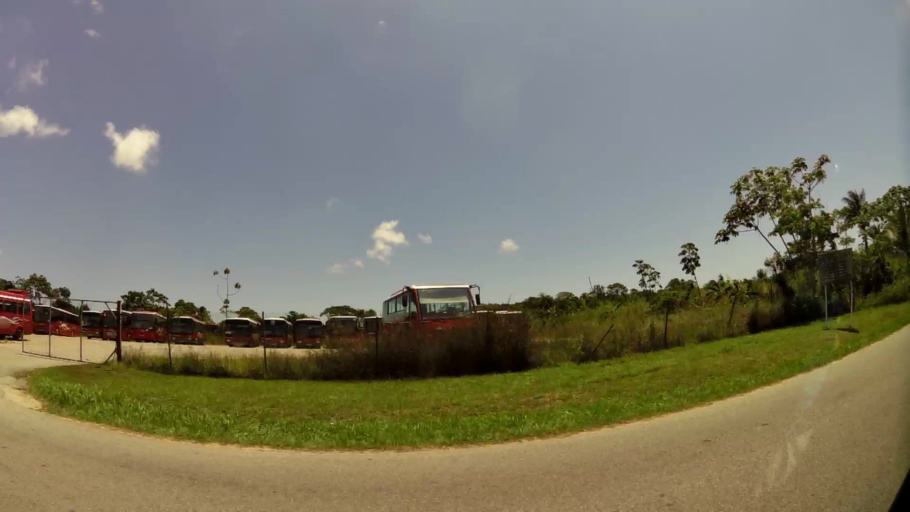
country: GF
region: Guyane
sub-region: Guyane
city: Cayenne
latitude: 4.8953
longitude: -52.3373
